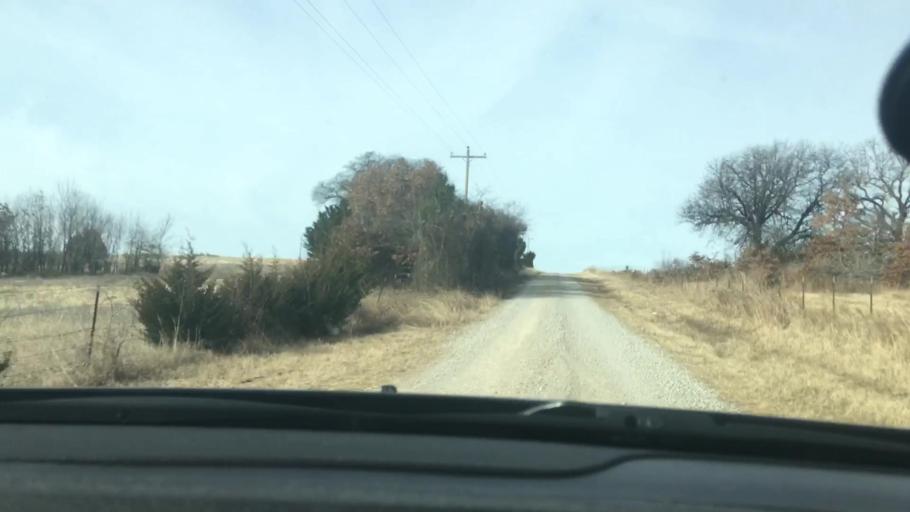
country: US
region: Oklahoma
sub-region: Garvin County
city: Wynnewood
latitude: 34.6374
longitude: -97.2413
